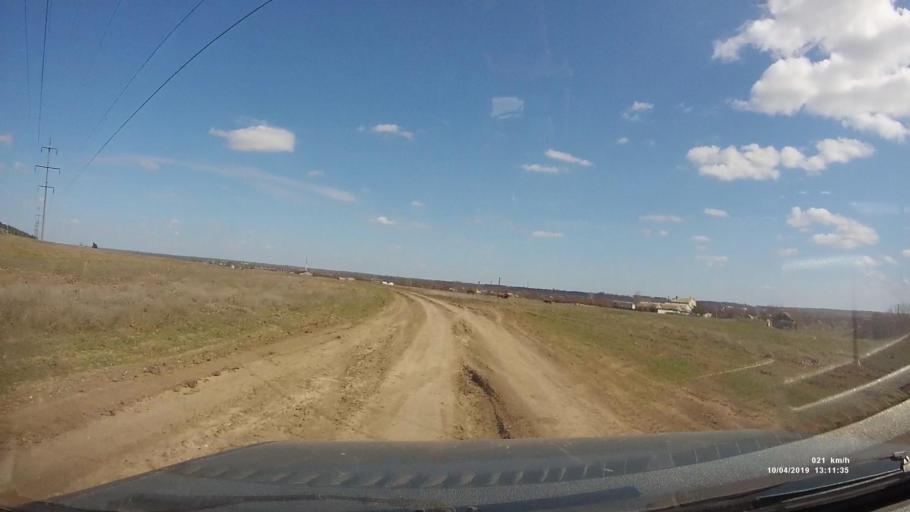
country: RU
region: Rostov
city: Masalovka
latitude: 48.4106
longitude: 40.2506
